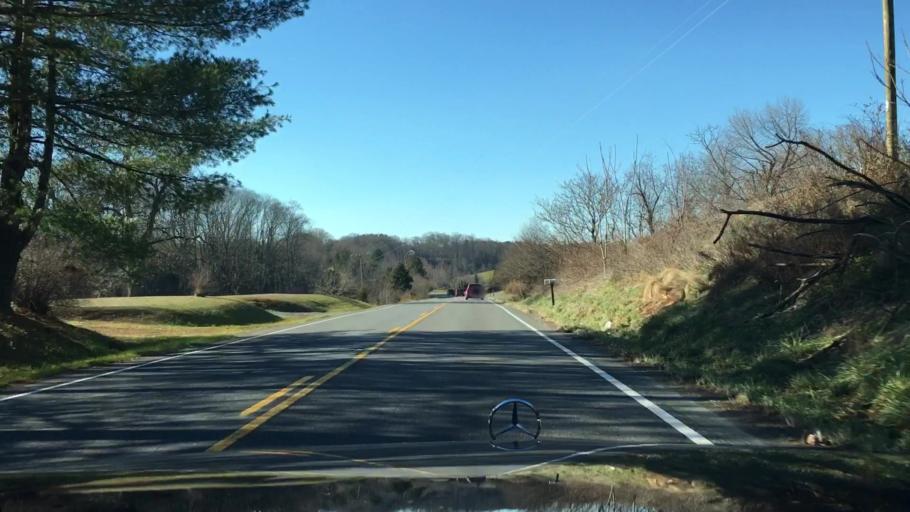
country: US
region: Virginia
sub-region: City of Bedford
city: Bedford
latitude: 37.2407
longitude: -79.5978
